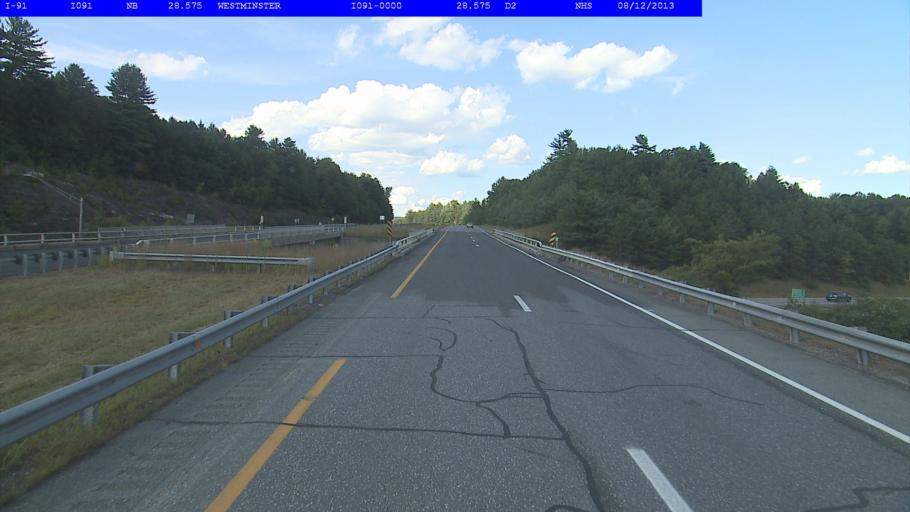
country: US
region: Vermont
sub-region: Windham County
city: Bellows Falls
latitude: 43.0906
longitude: -72.4565
